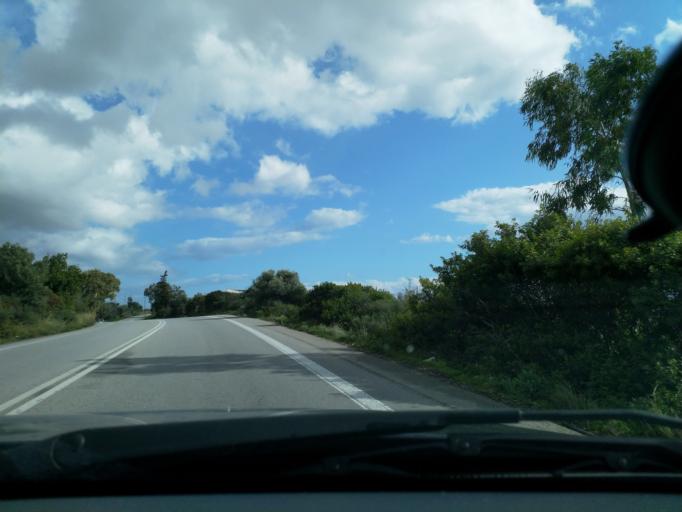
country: GR
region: Crete
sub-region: Nomos Chanias
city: Pithari
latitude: 35.5167
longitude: 24.0968
